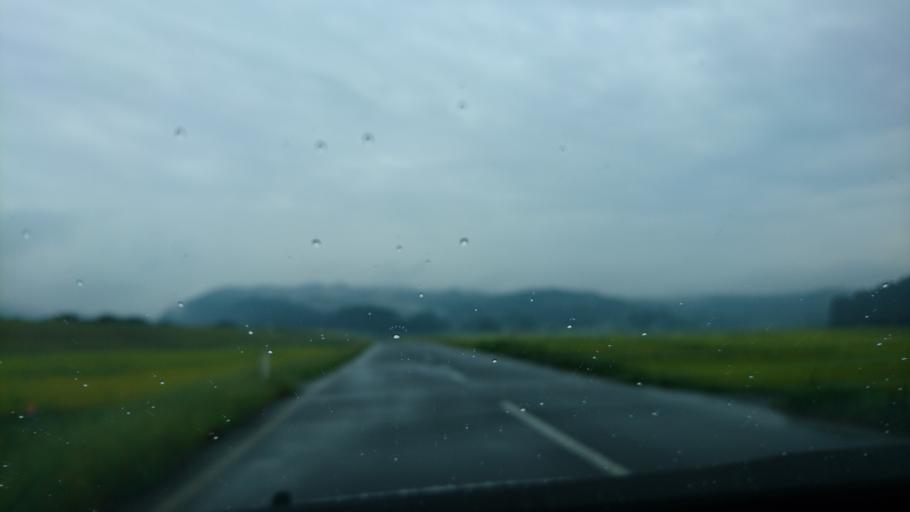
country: JP
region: Iwate
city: Ichinoseki
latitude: 38.8873
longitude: 141.2598
